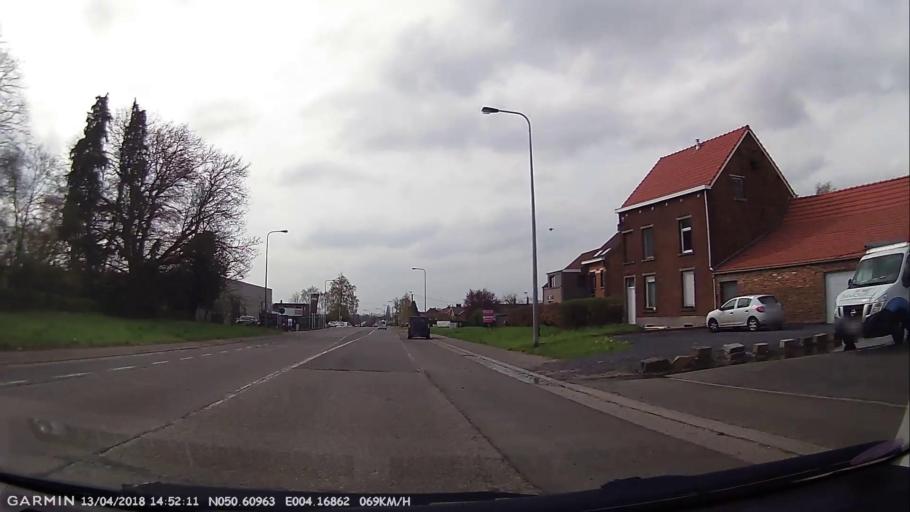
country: BE
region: Wallonia
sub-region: Province du Hainaut
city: Braine-le-Comte
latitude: 50.6097
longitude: 4.1683
